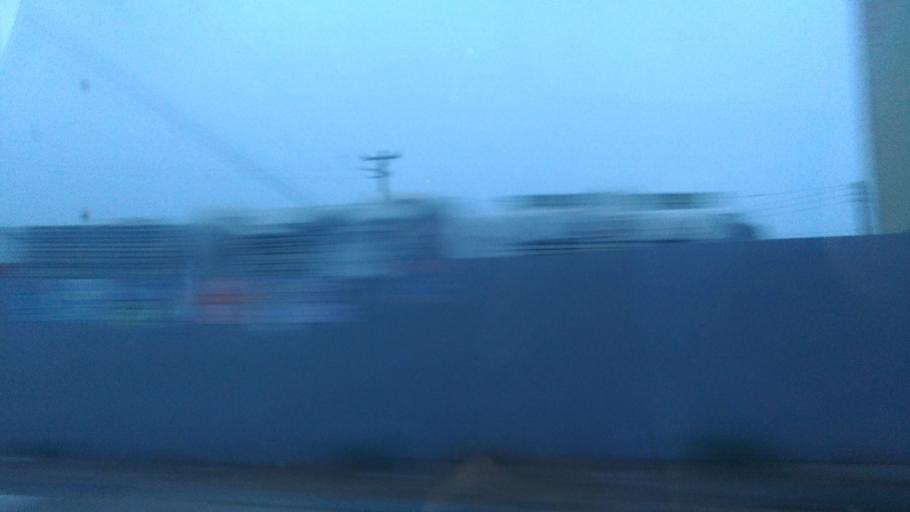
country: TW
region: Taiwan
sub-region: Miaoli
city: Miaoli
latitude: 24.5564
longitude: 120.7046
